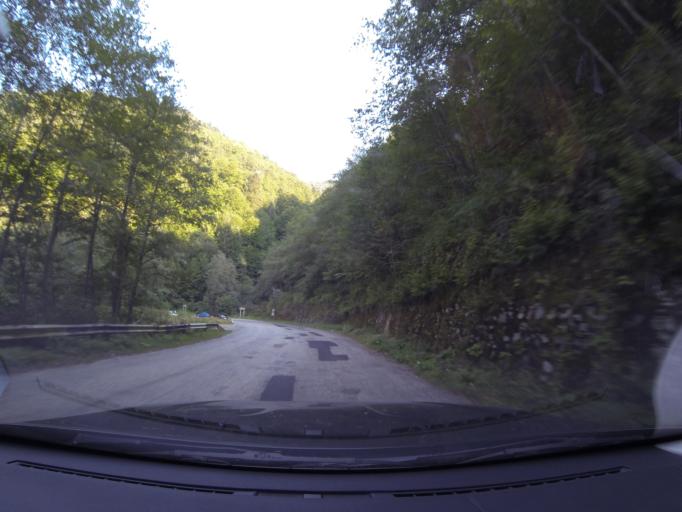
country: RO
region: Arges
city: Poenari
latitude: 45.3665
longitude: 24.6485
